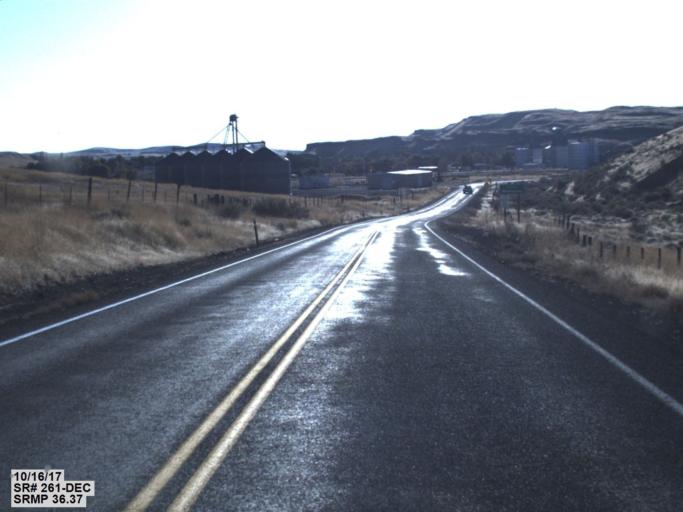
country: US
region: Washington
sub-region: Adams County
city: Ritzville
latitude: 46.7609
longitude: -118.2984
